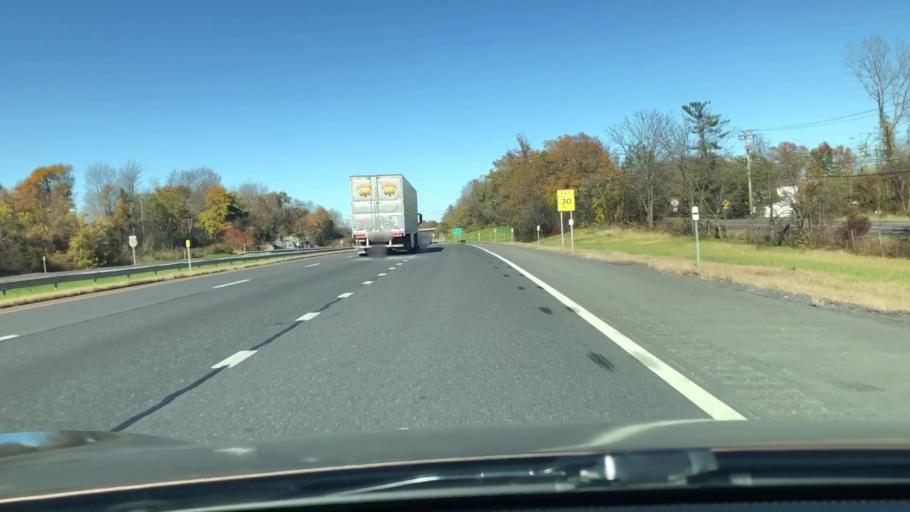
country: US
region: New York
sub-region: Ulster County
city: Saugerties
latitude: 42.0784
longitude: -73.9741
